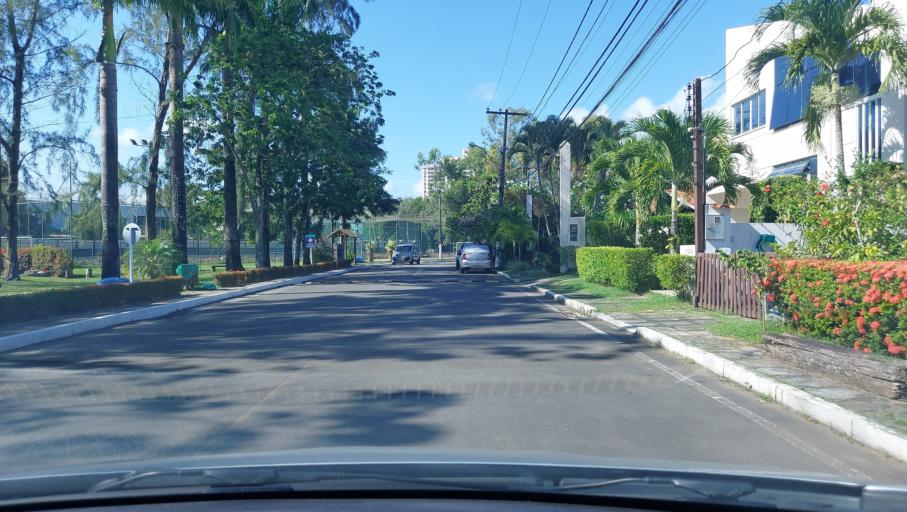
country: BR
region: Bahia
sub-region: Lauro De Freitas
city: Lauro de Freitas
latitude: -12.9422
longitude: -38.3835
